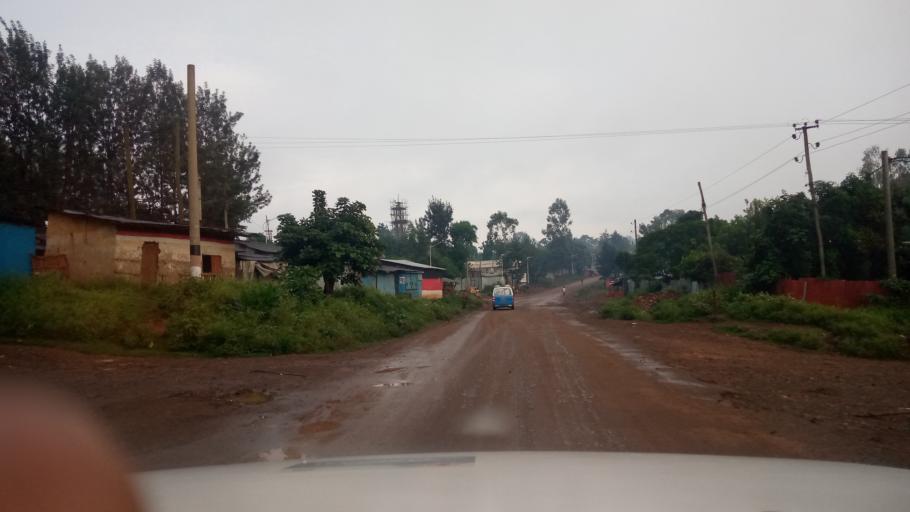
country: ET
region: Oromiya
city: Jima
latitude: 7.6939
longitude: 36.8197
